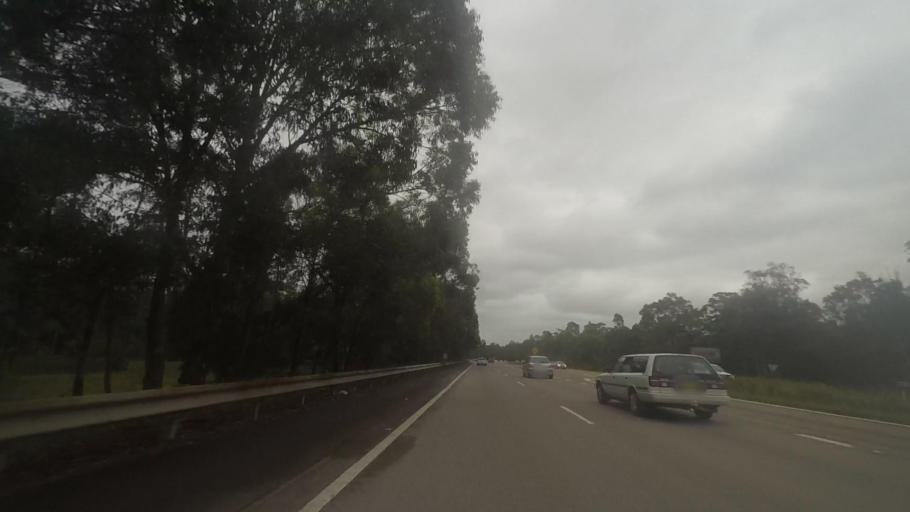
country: AU
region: New South Wales
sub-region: Port Stephens Shire
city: Raymond Terrace
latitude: -32.7009
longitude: 151.8030
